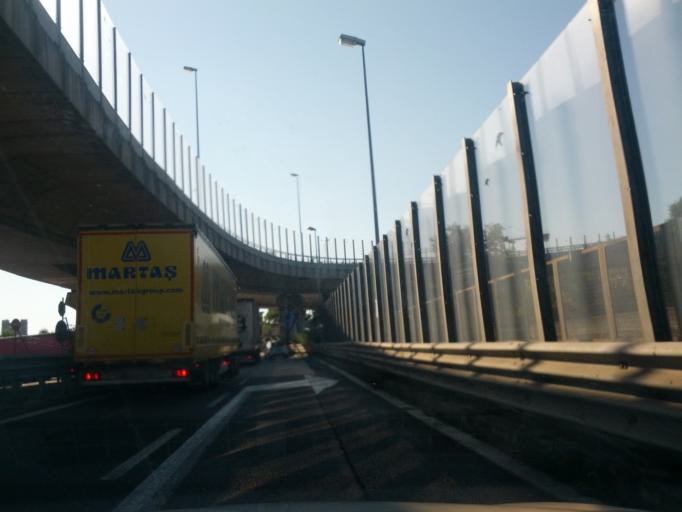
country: IT
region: Friuli Venezia Giulia
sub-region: Provincia di Trieste
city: Trieste
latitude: 45.6378
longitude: 13.7656
